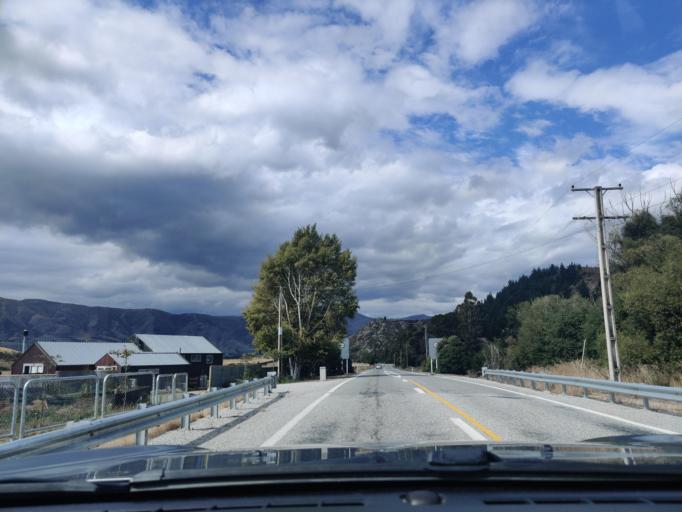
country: NZ
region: Otago
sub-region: Queenstown-Lakes District
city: Wanaka
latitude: -44.7507
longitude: 169.2753
